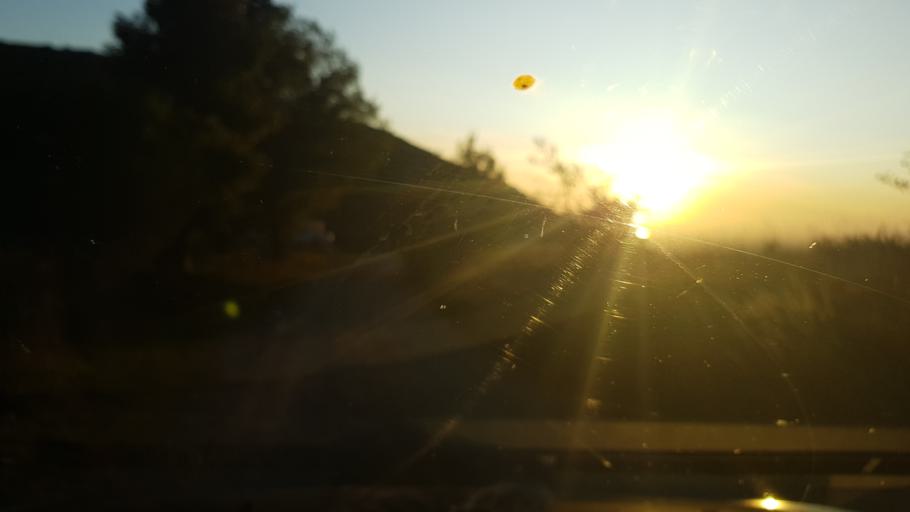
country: SI
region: Vipava
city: Vipava
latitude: 45.7842
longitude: 14.0376
